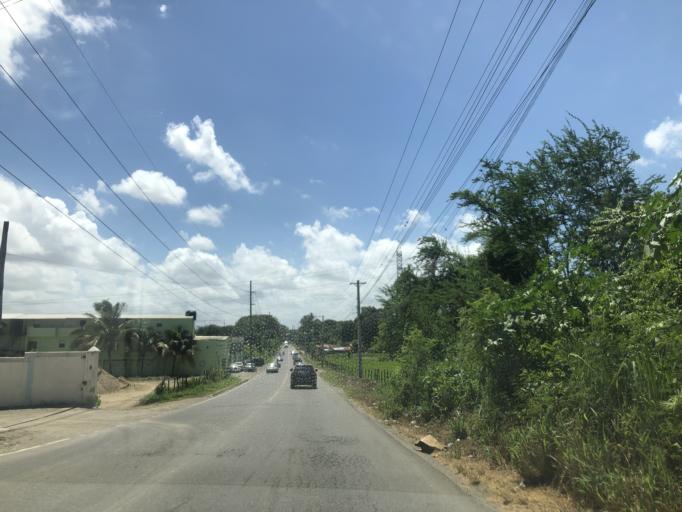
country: DO
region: Santiago
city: Santiago de los Caballeros
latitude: 19.4516
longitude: -70.7551
